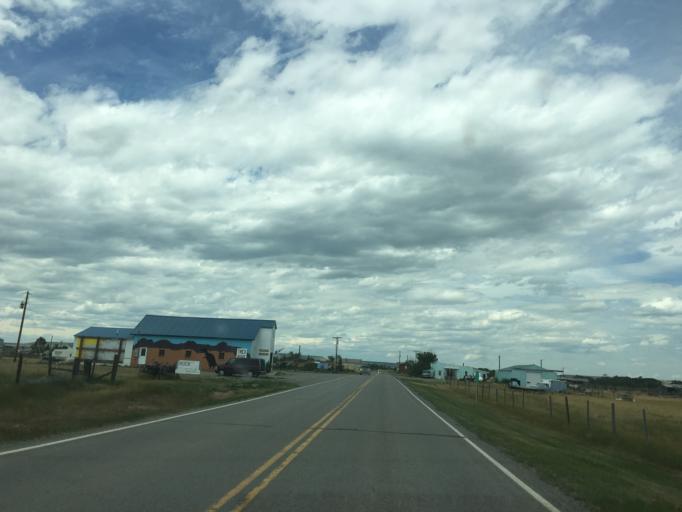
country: US
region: Montana
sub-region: Teton County
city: Choteau
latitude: 47.9751
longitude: -112.3103
